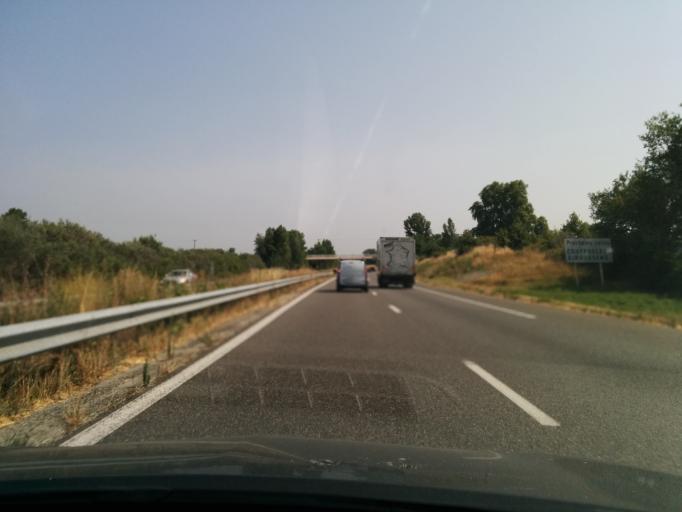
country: FR
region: Midi-Pyrenees
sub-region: Departement du Tarn
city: Saint-Sulpice-la-Pointe
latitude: 43.7740
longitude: 1.7270
